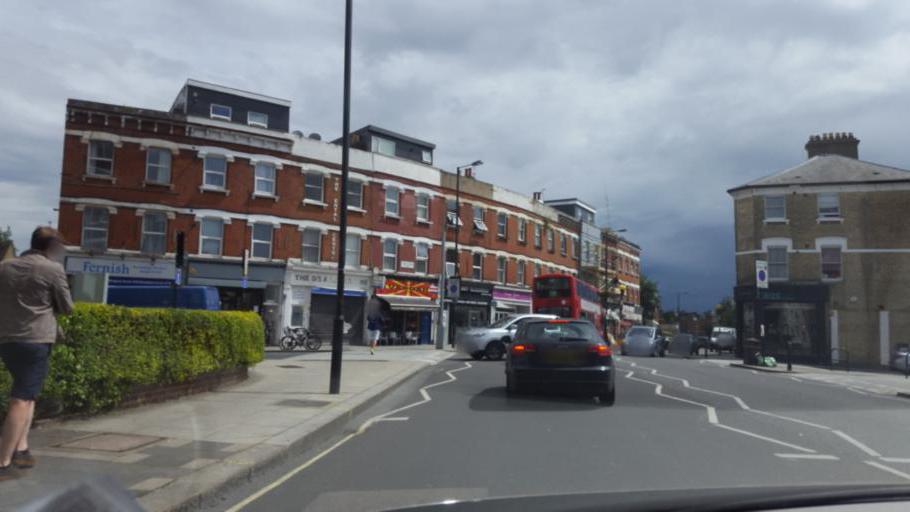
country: GB
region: England
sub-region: Greater London
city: Hammersmith
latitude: 51.5046
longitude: -0.2439
